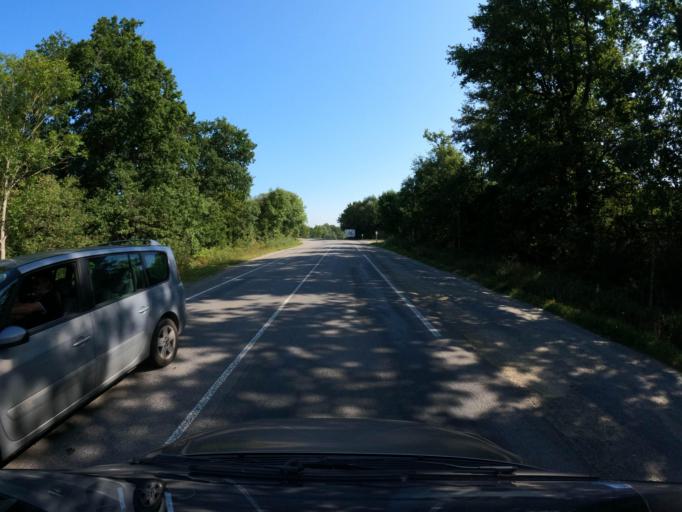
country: FR
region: Pays de la Loire
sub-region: Departement de la Loire-Atlantique
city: La Chevroliere
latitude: 47.0765
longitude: -1.5650
